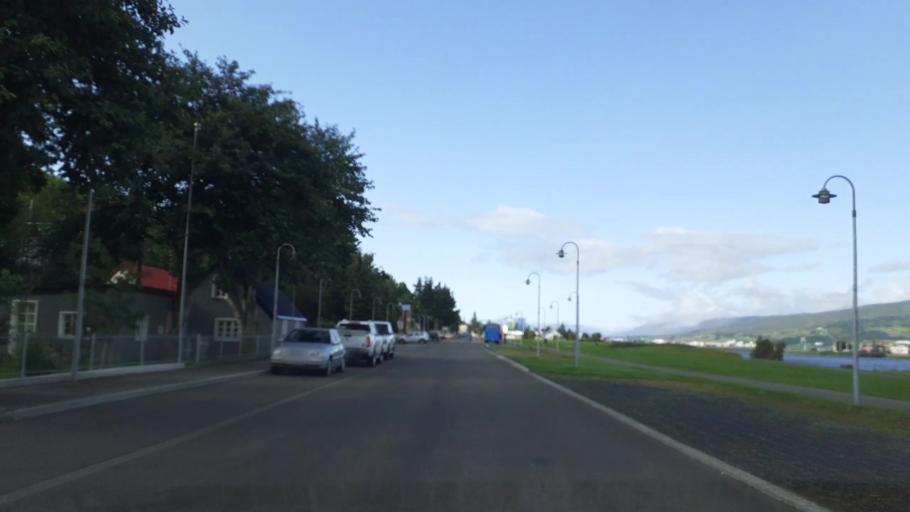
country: IS
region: Northeast
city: Akureyri
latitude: 65.6656
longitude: -18.0845
